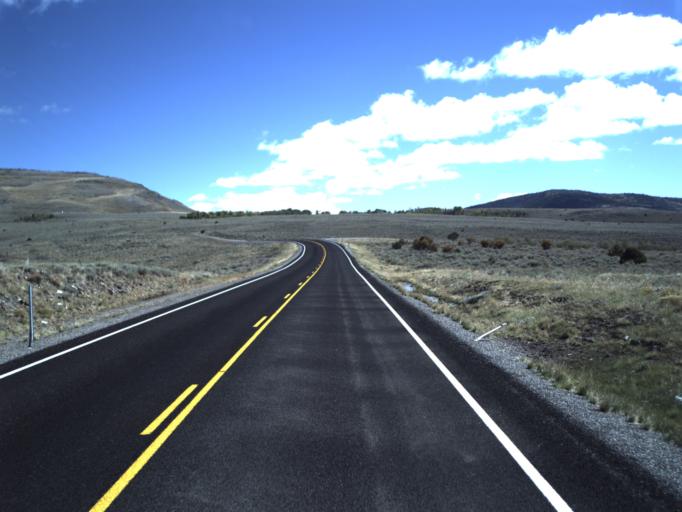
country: US
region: Utah
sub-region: Wayne County
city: Loa
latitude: 38.4992
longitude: -111.8031
